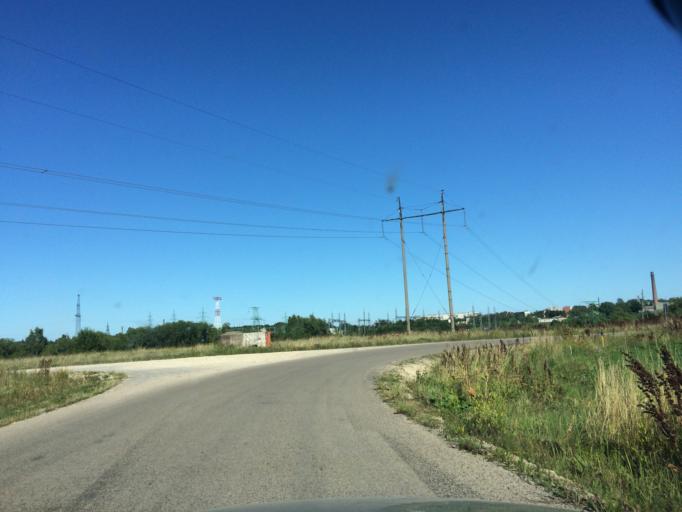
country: LV
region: Rezekne
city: Rezekne
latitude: 56.5097
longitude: 27.3086
